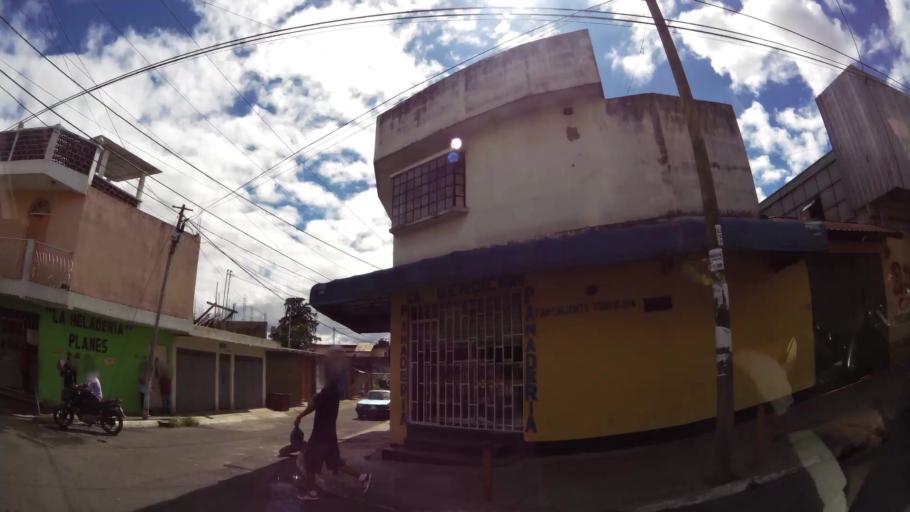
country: GT
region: Guatemala
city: Chinautla
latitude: 14.6827
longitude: -90.5448
